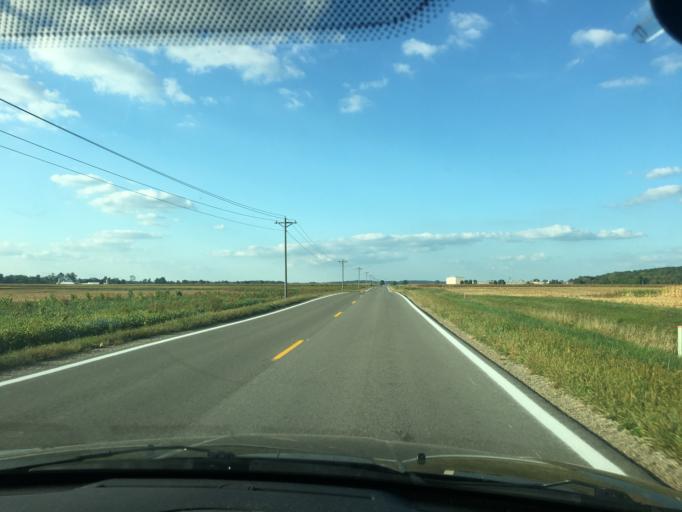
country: US
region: Ohio
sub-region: Champaign County
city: Urbana
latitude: 40.1749
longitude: -83.7829
